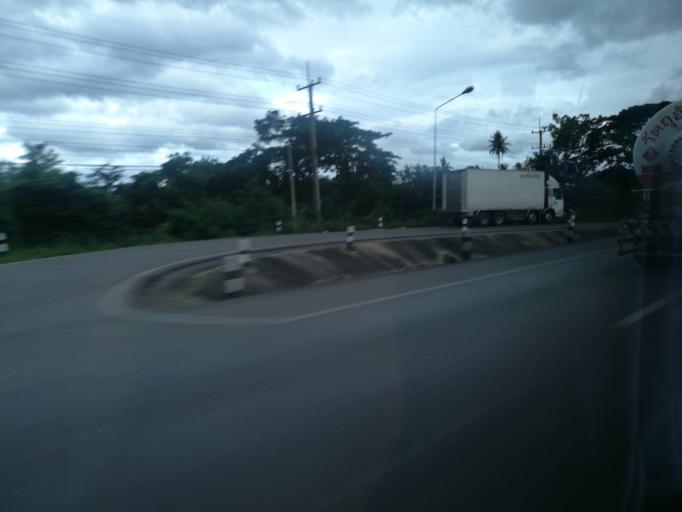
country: TH
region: Prachuap Khiri Khan
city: Kui Buri
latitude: 12.1626
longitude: 99.8446
